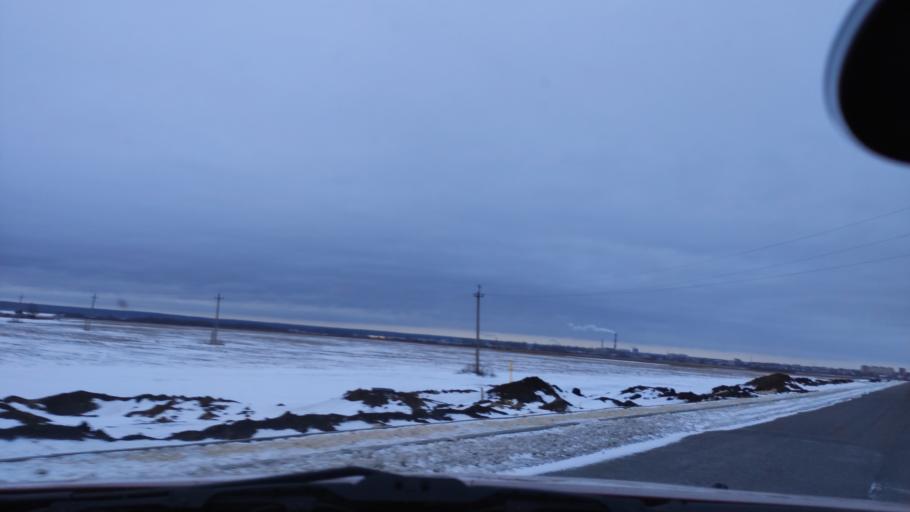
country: RU
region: Tambov
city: Donskoye
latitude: 52.7836
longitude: 41.4334
